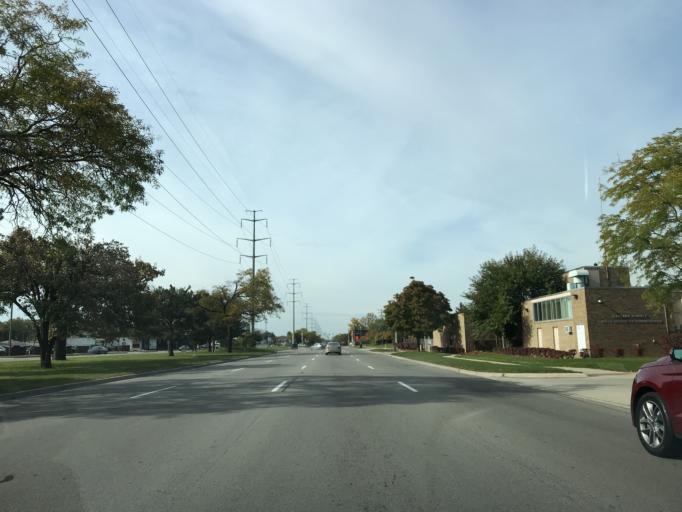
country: US
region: Michigan
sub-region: Oakland County
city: Southfield
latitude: 42.4435
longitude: -83.2630
